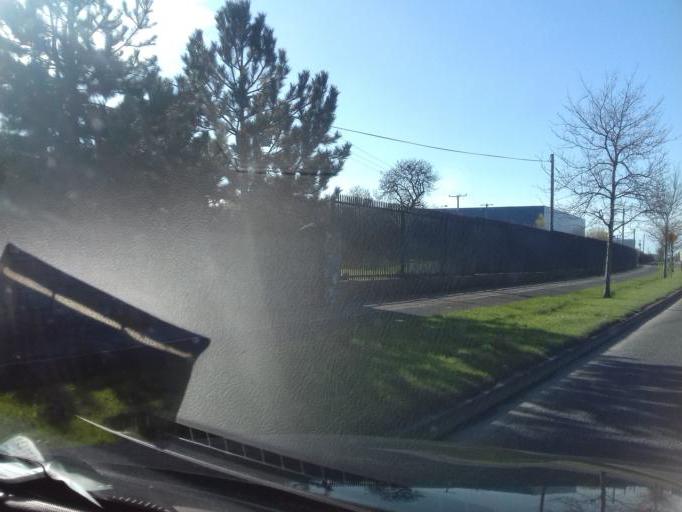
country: IE
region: Leinster
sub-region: Dublin City
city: Finglas
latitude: 53.3999
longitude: -6.3337
